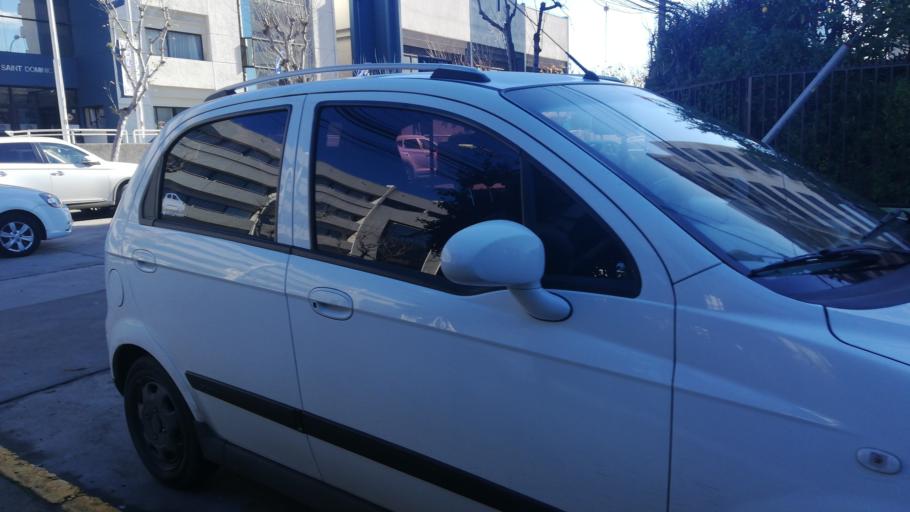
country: CL
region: Valparaiso
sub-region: Provincia de Valparaiso
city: Vina del Mar
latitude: -33.0172
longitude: -71.5477
